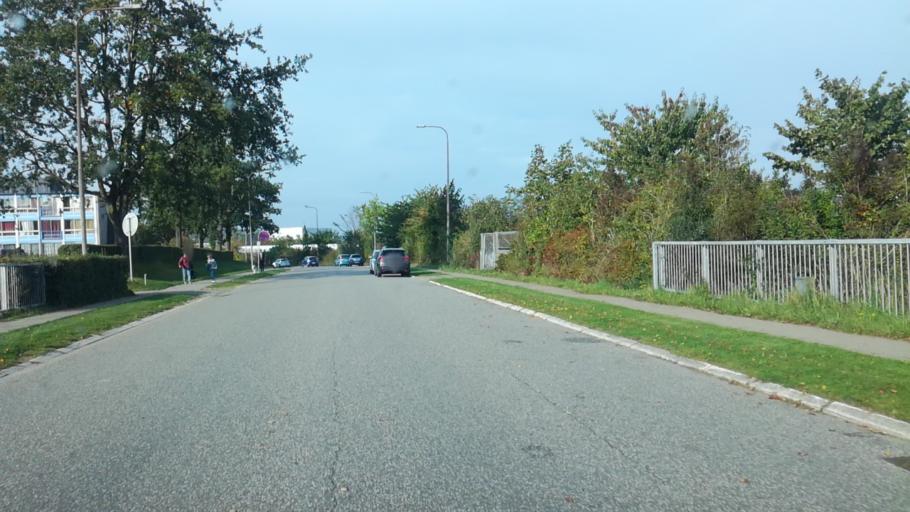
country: DK
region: South Denmark
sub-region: Fredericia Kommune
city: Fredericia
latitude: 55.5729
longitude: 9.7220
